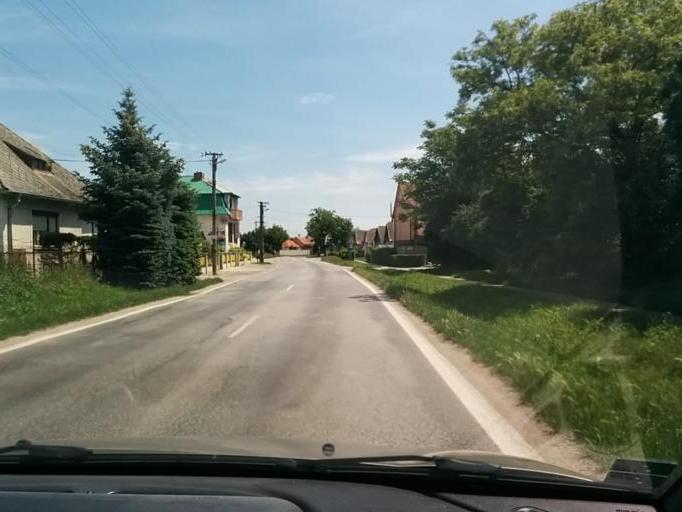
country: SK
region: Trnavsky
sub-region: Okres Galanta
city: Galanta
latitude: 48.2503
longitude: 17.8202
